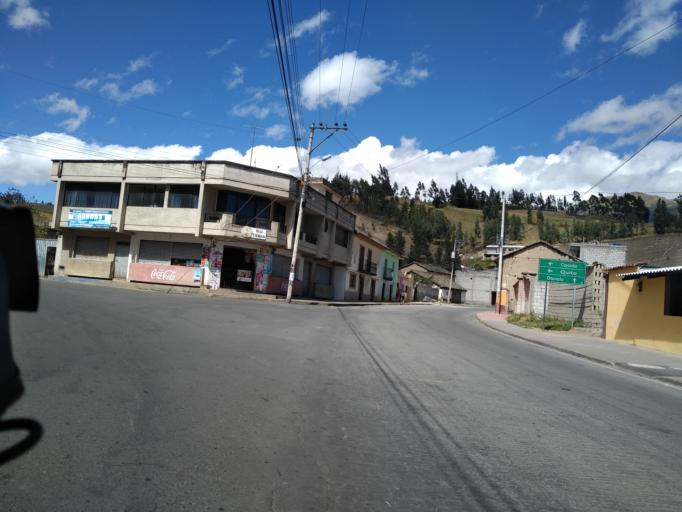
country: EC
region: Imbabura
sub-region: Canton Otavalo
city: Otavalo
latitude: 0.1775
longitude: -78.2051
